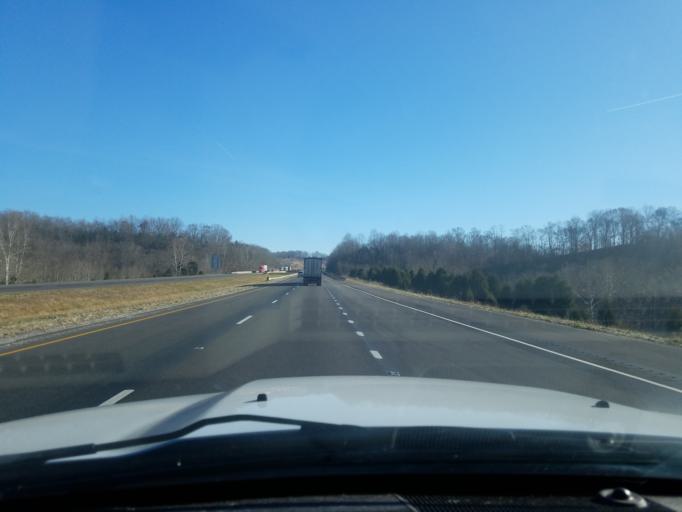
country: US
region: Indiana
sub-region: Crawford County
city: English
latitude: 38.2429
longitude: -86.4628
